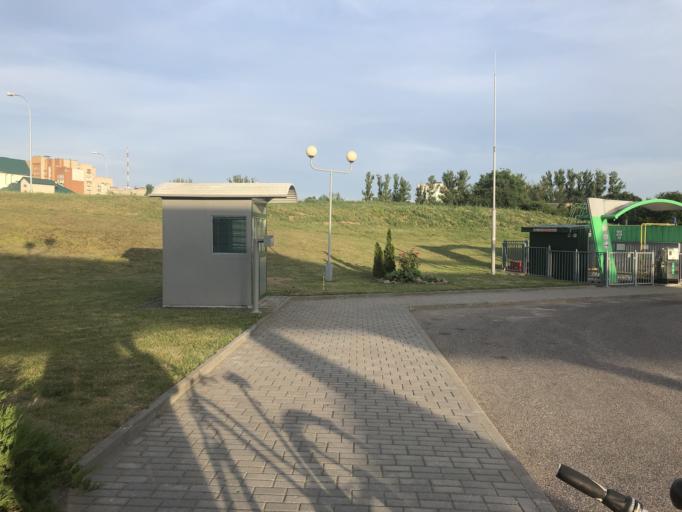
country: BY
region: Grodnenskaya
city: Hrodna
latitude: 53.7105
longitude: 23.7968
